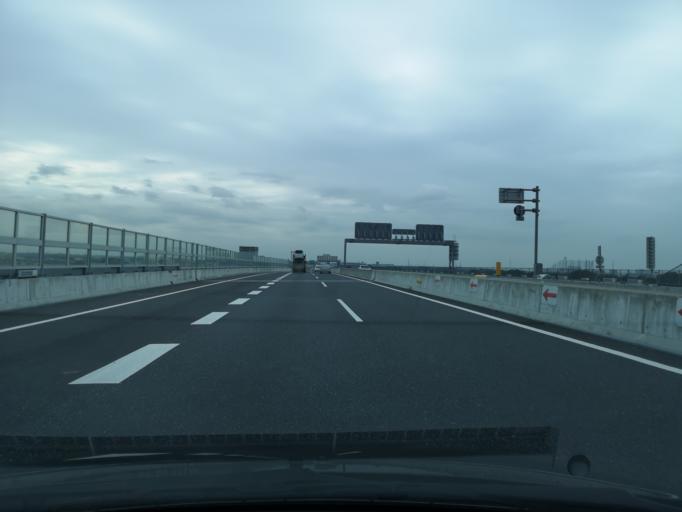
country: JP
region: Kanagawa
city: Atsugi
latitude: 35.4051
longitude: 139.3739
